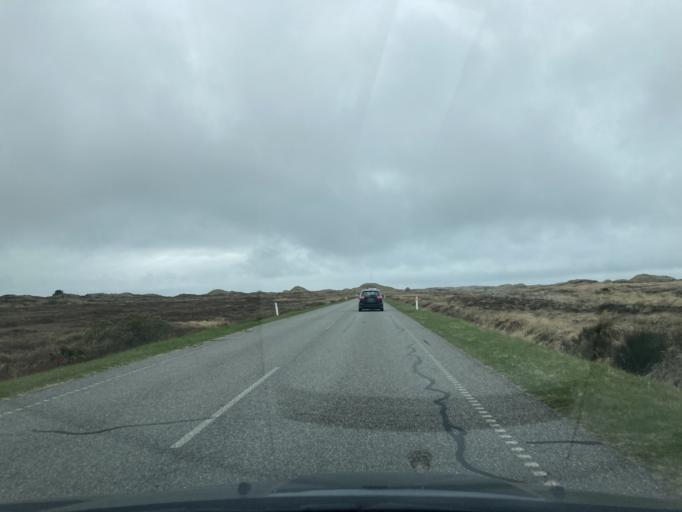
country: DK
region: North Denmark
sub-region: Thisted Kommune
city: Hurup
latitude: 56.9275
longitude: 8.3507
